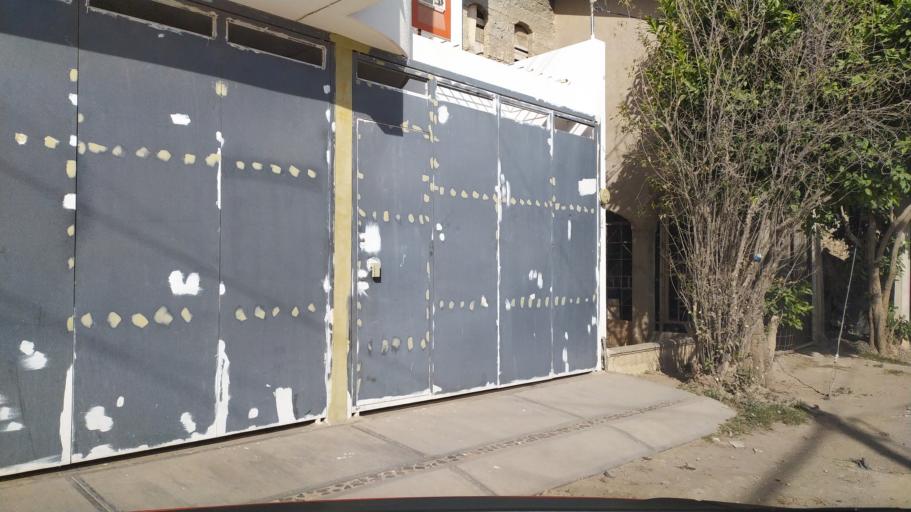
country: MX
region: Jalisco
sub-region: Tlajomulco de Zuniga
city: Palomar
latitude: 20.6309
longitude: -103.4710
